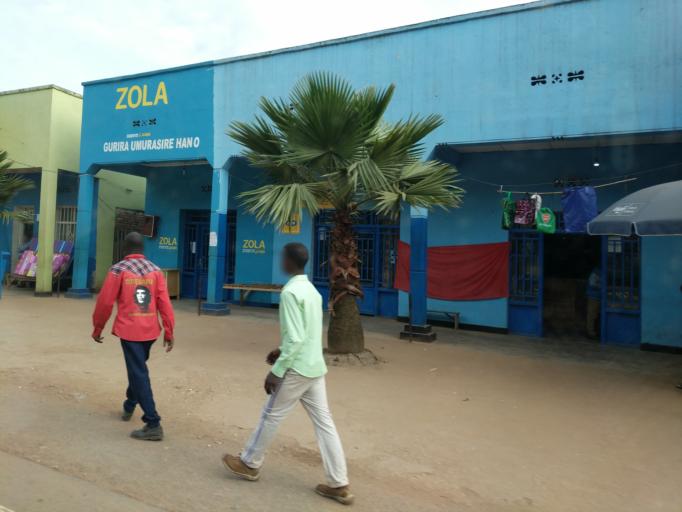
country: RW
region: Northern Province
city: Musanze
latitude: -1.6475
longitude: 29.7915
